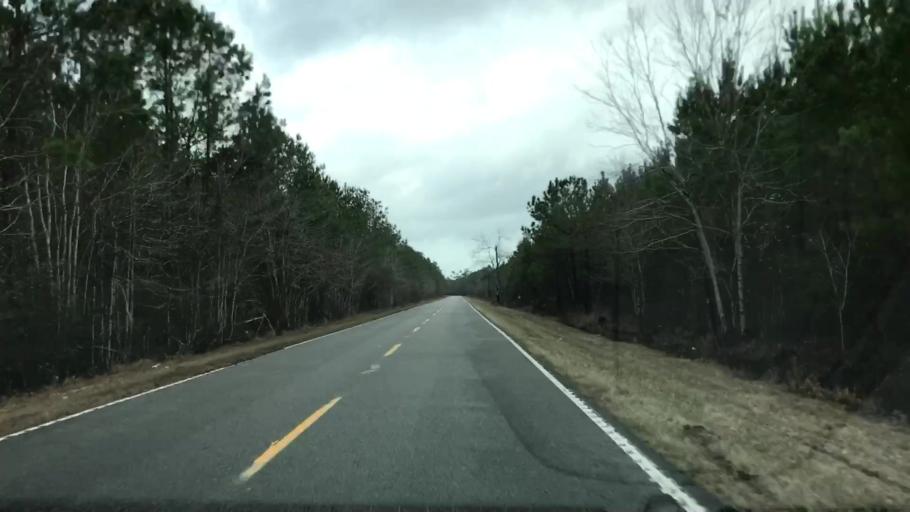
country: US
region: South Carolina
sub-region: Georgetown County
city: Murrells Inlet
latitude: 33.6284
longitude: -79.2447
